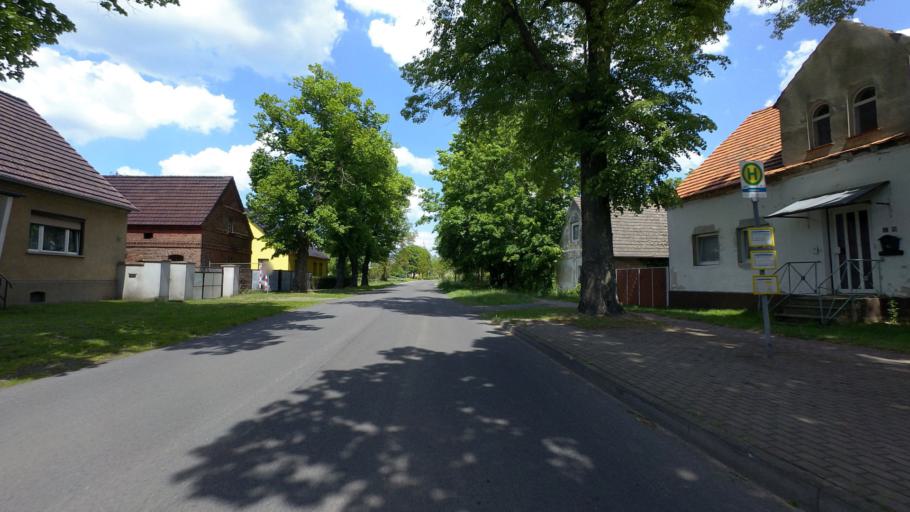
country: DE
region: Brandenburg
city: Straupitz
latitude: 51.9319
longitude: 14.1680
